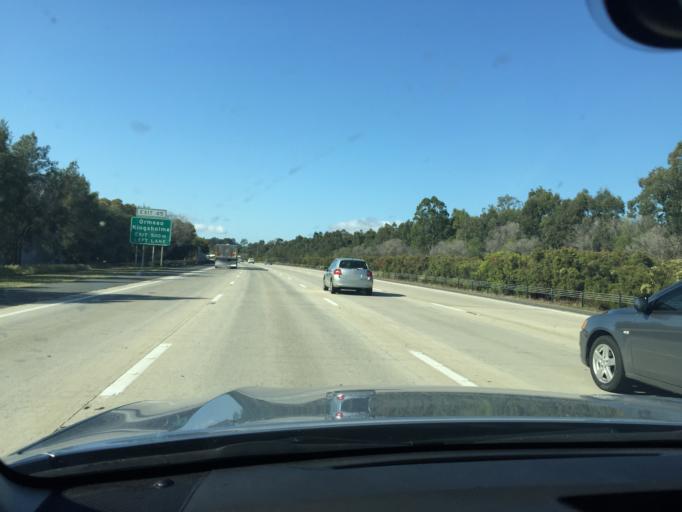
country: AU
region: Queensland
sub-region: Gold Coast
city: Ormeau Hills
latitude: -27.7771
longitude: 153.2523
